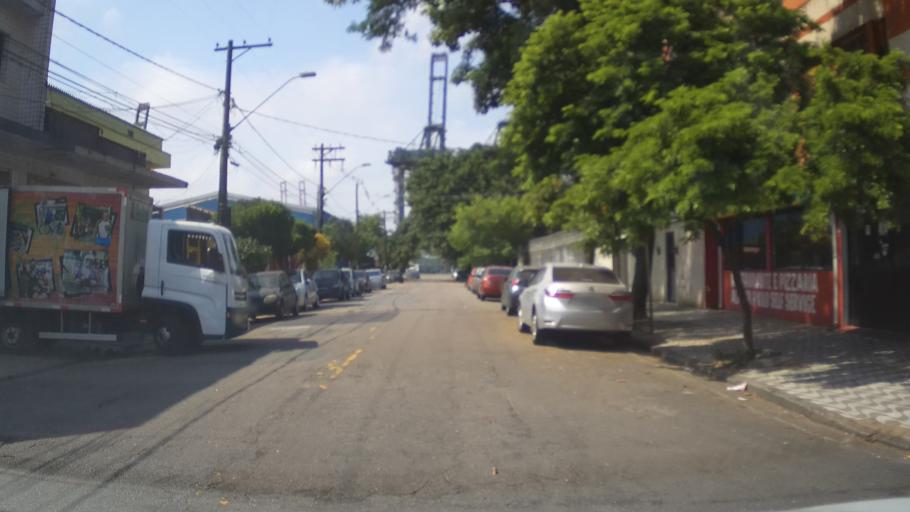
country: BR
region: Sao Paulo
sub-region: Santos
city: Santos
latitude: -23.9766
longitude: -46.2959
